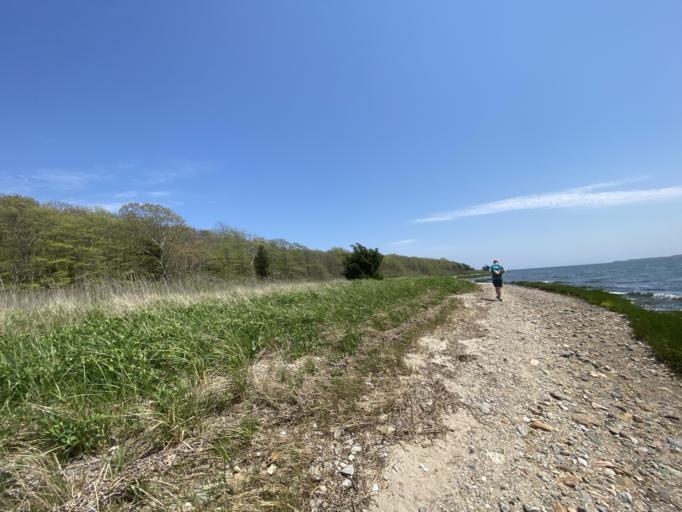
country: US
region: Massachusetts
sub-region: Plymouth County
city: Mattapoisett
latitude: 41.6278
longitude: -70.8419
